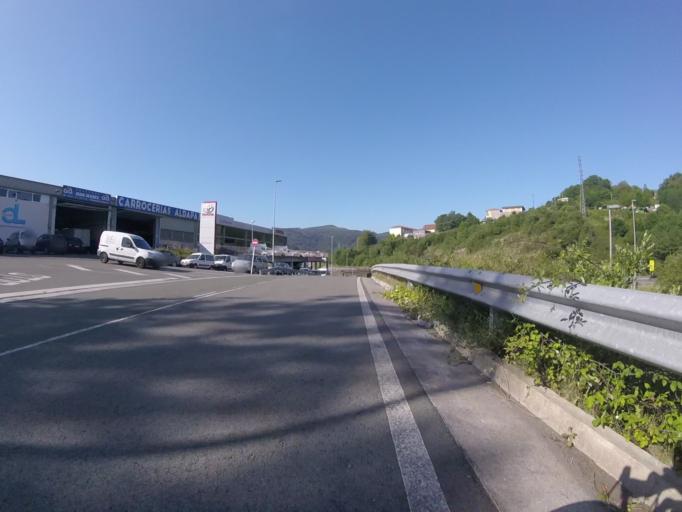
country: ES
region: Basque Country
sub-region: Provincia de Guipuzcoa
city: Errenteria
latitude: 43.3142
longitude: -1.9169
